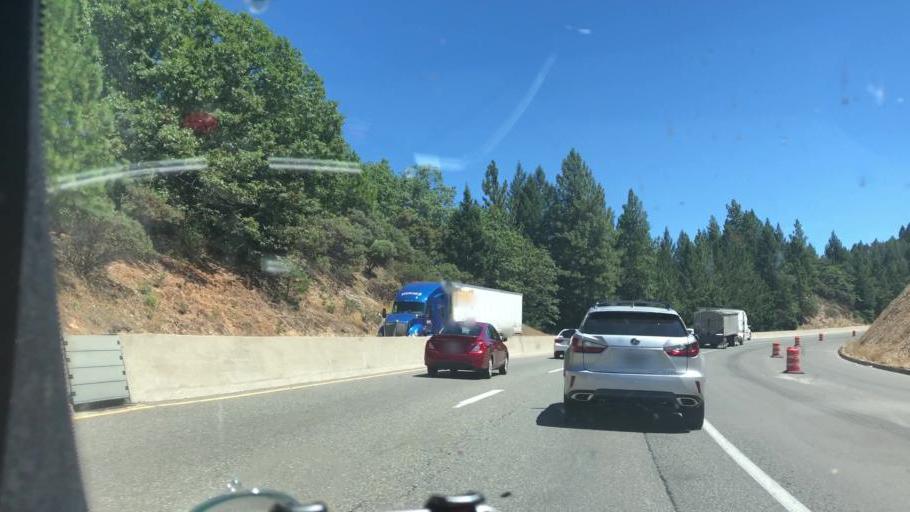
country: US
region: California
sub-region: Placer County
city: Colfax
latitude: 39.1320
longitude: -120.9350
